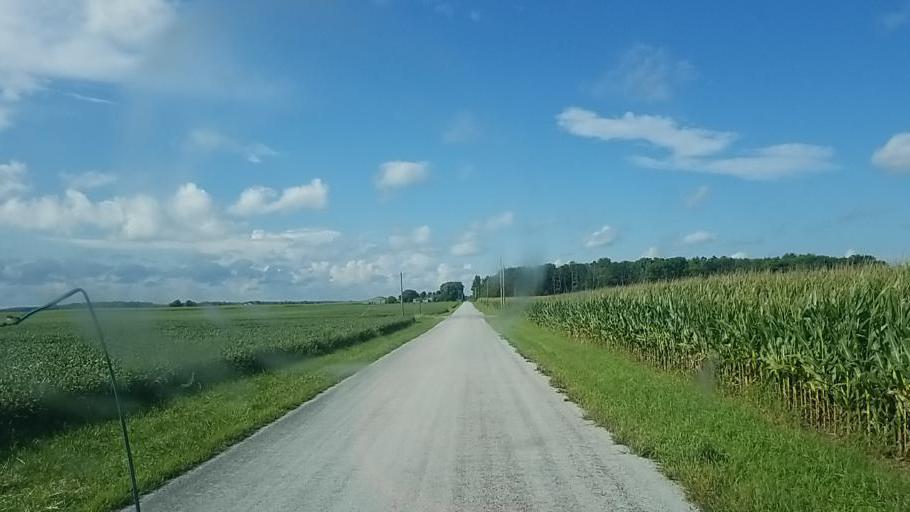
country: US
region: Ohio
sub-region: Hardin County
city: Kenton
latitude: 40.6867
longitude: -83.5309
